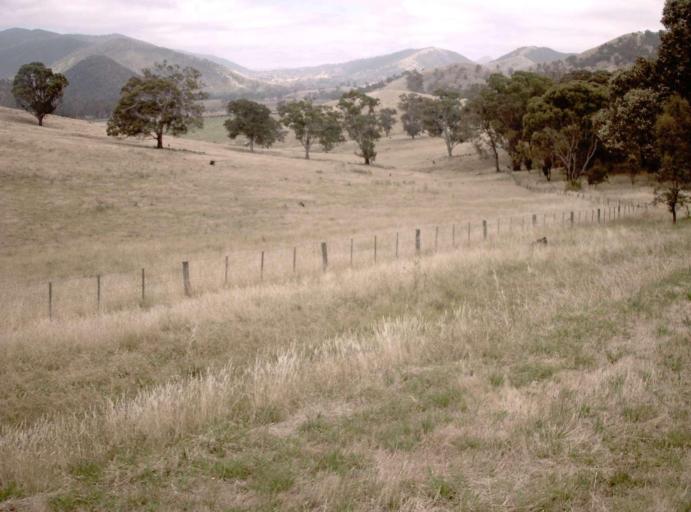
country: AU
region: Victoria
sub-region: Wellington
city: Heyfield
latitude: -37.6849
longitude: 146.6568
